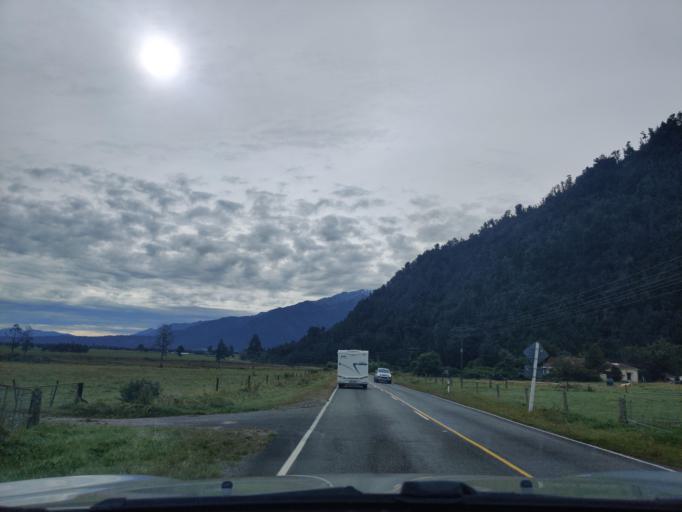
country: NZ
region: West Coast
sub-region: Westland District
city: Hokitika
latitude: -43.2798
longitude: 170.3403
